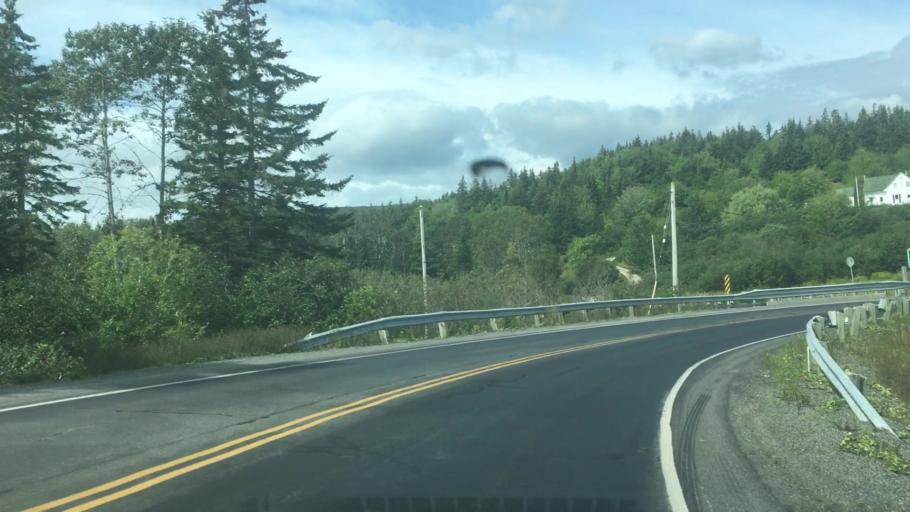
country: CA
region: Nova Scotia
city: Sydney Mines
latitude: 46.2636
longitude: -60.6240
